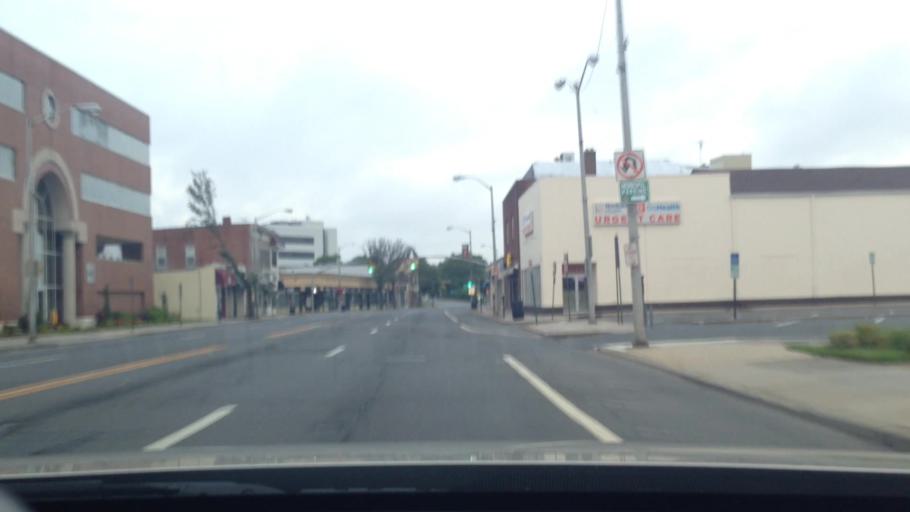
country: US
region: New York
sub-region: Nassau County
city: Rockville Centre
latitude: 40.6563
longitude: -73.6462
